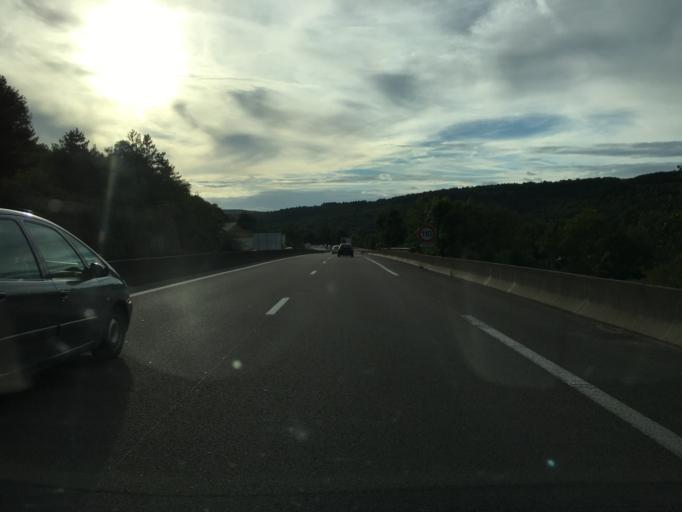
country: FR
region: Bourgogne
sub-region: Departement de la Cote-d'Or
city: Plombieres-les-Dijon
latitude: 47.3369
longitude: 4.9679
